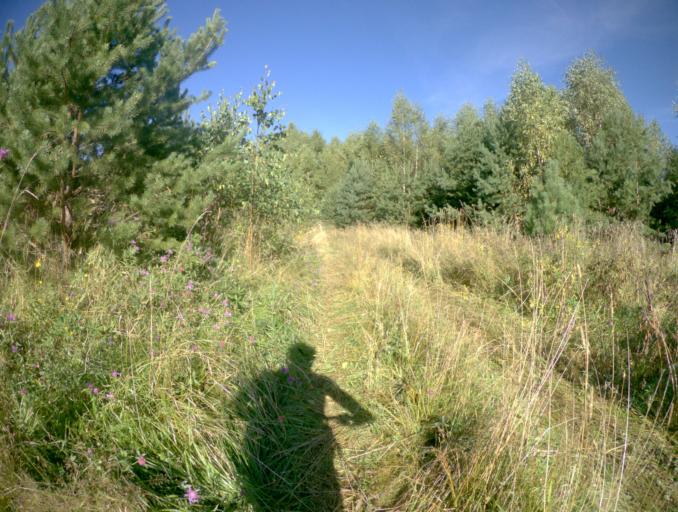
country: RU
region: Vladimir
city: Nikologory
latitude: 56.1547
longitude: 41.9498
